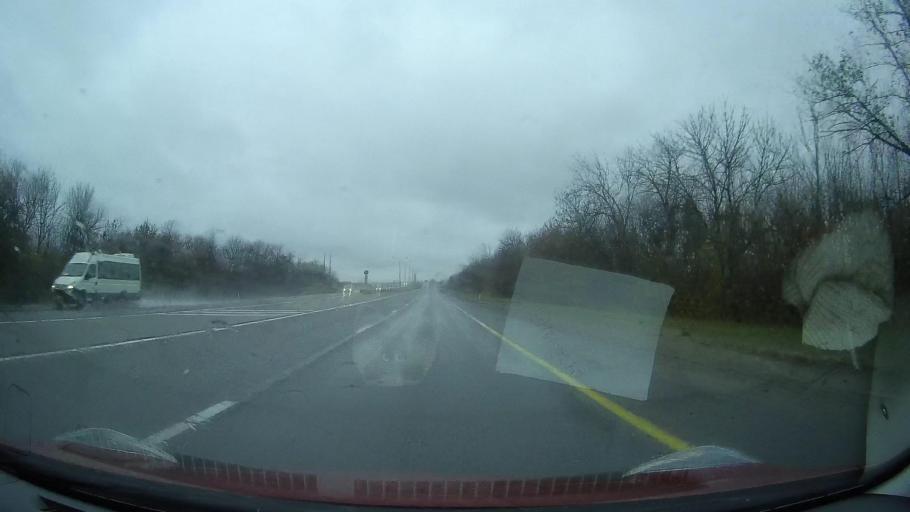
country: RU
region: Stavropol'skiy
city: Nevinnomyssk
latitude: 44.6353
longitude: 42.0019
